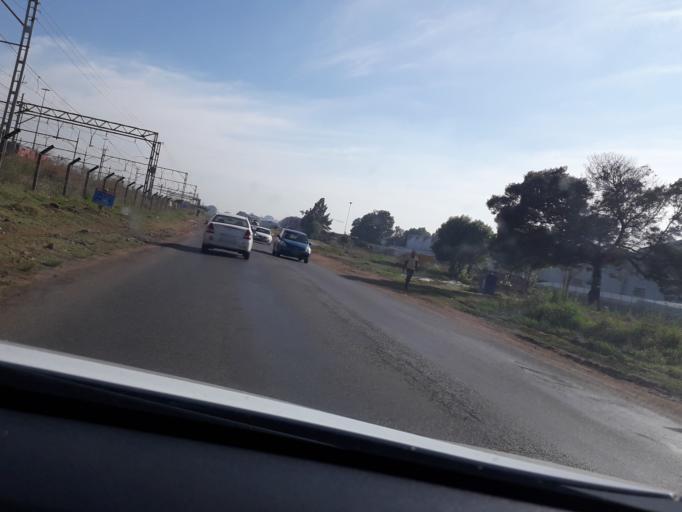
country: ZA
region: Gauteng
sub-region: Ekurhuleni Metropolitan Municipality
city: Boksburg
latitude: -26.1555
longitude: 28.2130
